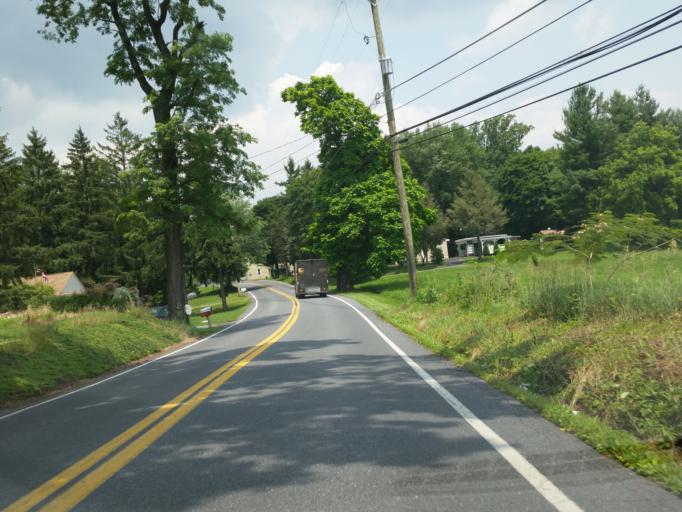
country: US
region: Pennsylvania
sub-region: Lebanon County
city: Campbelltown
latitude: 40.2609
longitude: -76.5882
